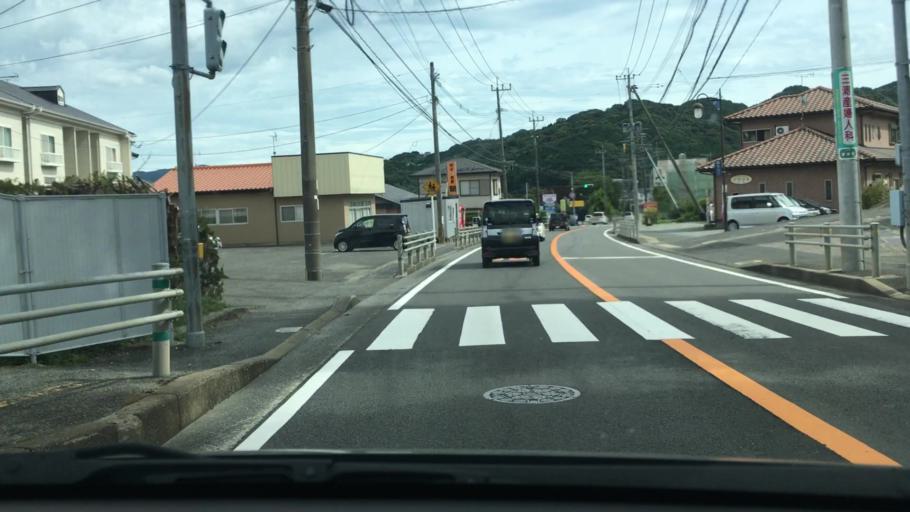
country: JP
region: Nagasaki
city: Togitsu
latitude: 32.8995
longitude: 129.7809
